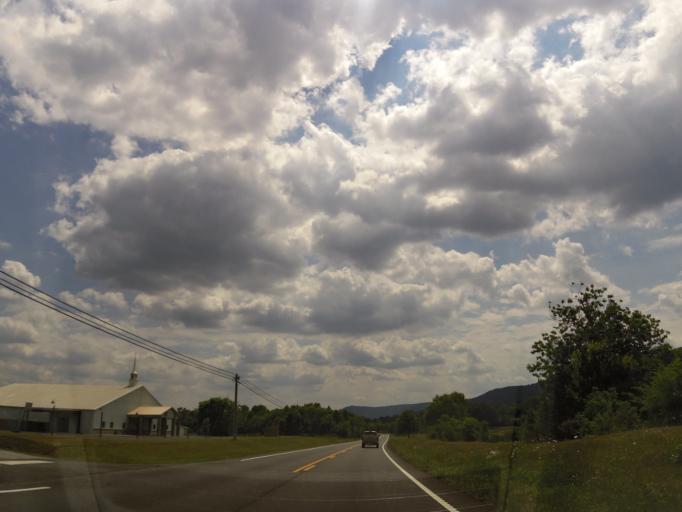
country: US
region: Tennessee
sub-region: Sequatchie County
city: Dunlap
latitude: 35.4469
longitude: -85.3399
